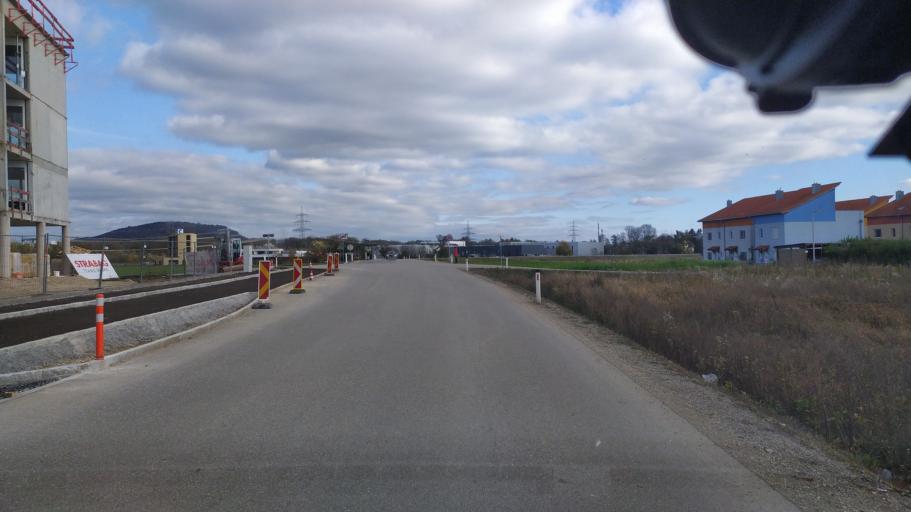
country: AT
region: Upper Austria
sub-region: Politischer Bezirk Urfahr-Umgebung
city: Steyregg
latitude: 48.2538
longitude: 14.3703
